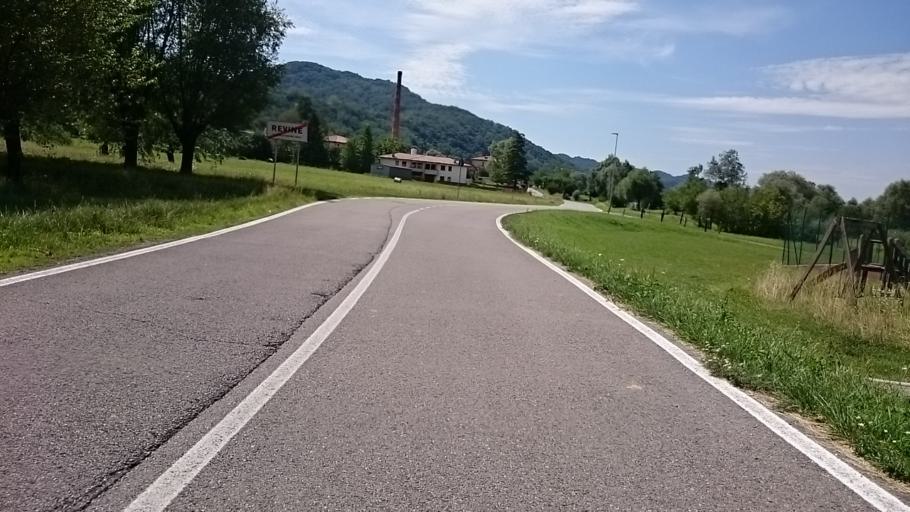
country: IT
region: Veneto
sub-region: Provincia di Treviso
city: Revine
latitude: 45.9969
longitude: 12.2523
